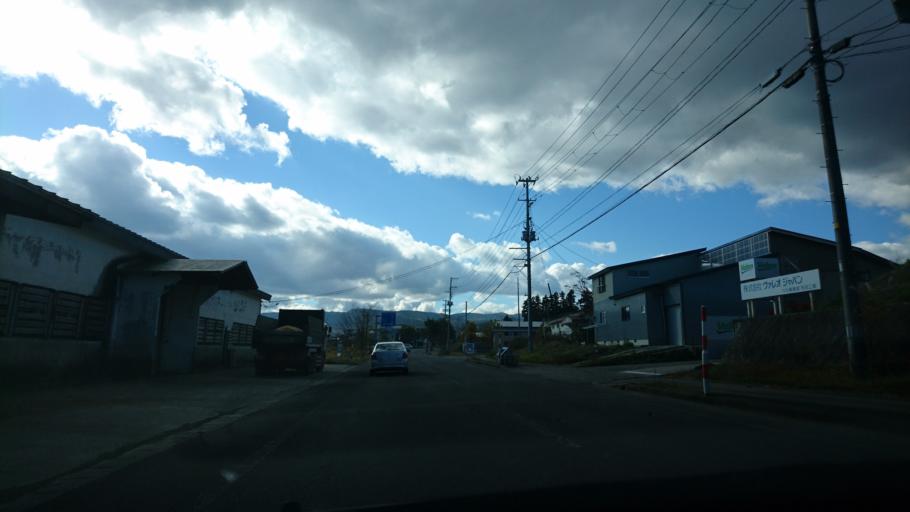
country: JP
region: Akita
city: Yuzawa
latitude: 39.2760
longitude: 140.3962
